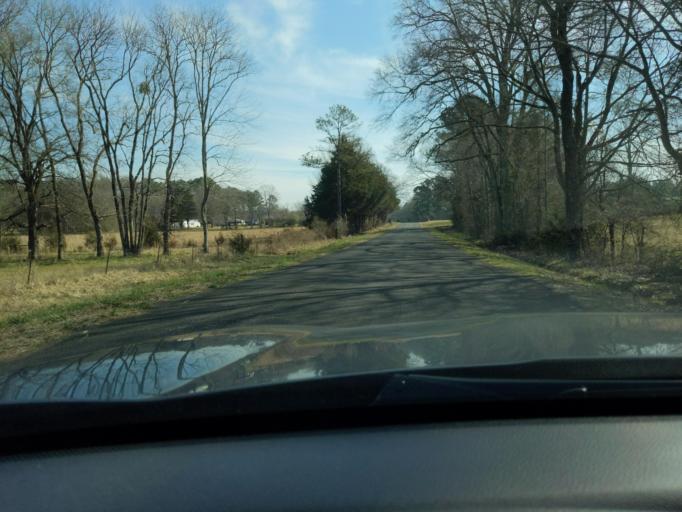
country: US
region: South Carolina
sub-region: Abbeville County
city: Calhoun Falls
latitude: 34.0941
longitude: -82.5635
